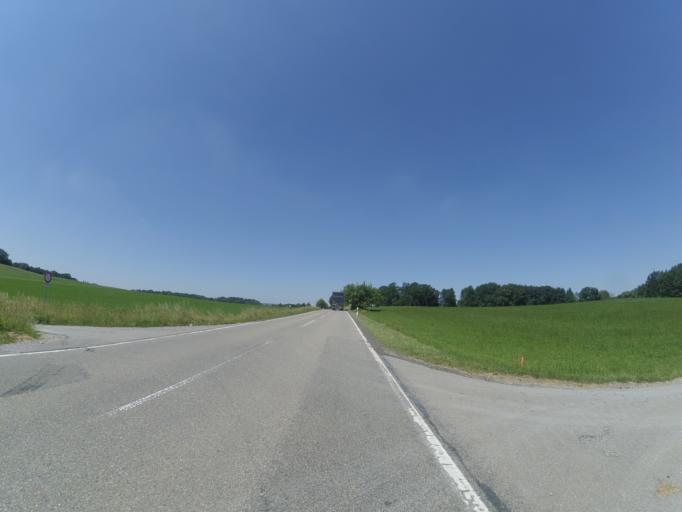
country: DE
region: Baden-Wuerttemberg
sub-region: Tuebingen Region
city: Bad Waldsee
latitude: 47.9097
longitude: 9.7726
